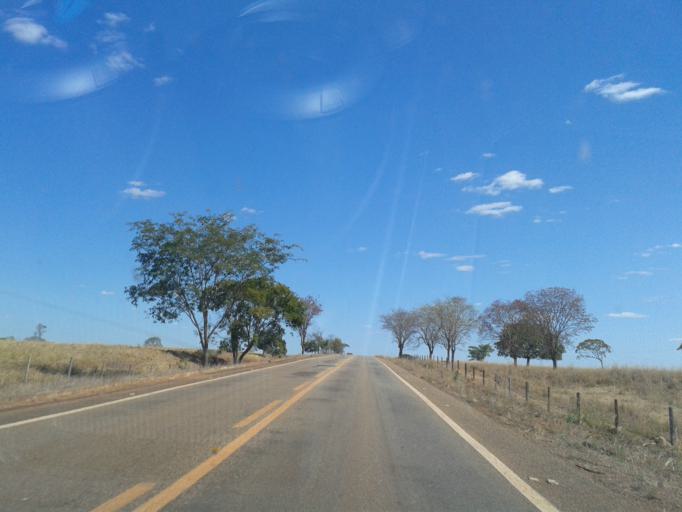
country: BR
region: Goias
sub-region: Sao Miguel Do Araguaia
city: Sao Miguel do Araguaia
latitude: -13.4395
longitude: -50.2878
